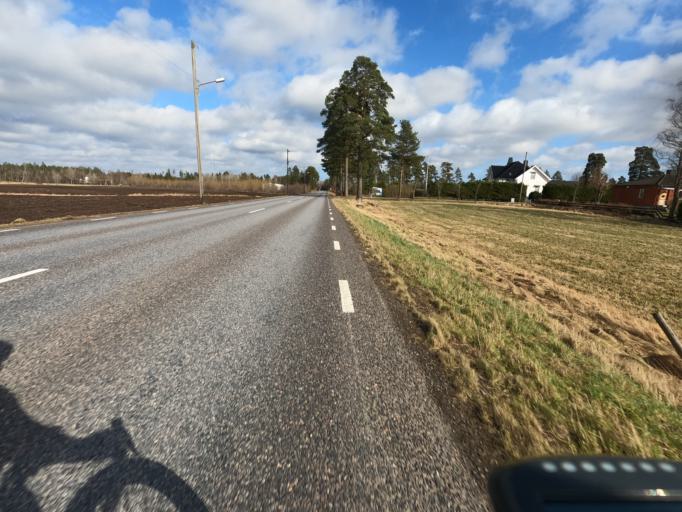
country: SE
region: Kronoberg
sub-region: Alvesta Kommun
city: Vislanda
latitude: 56.7860
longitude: 14.4762
